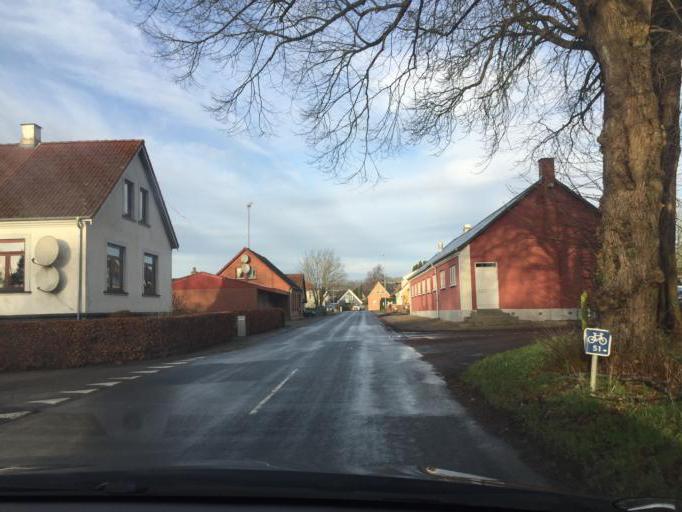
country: DK
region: South Denmark
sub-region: Faaborg-Midtfyn Kommune
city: Ringe
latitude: 55.1998
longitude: 10.4105
